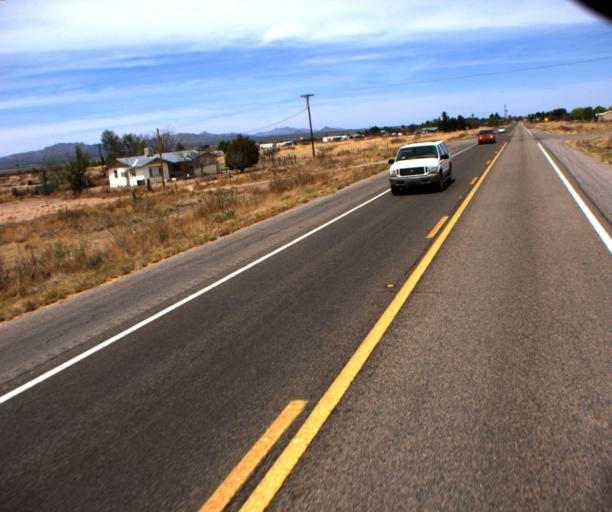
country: US
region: Arizona
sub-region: Cochise County
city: Bisbee
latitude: 31.6701
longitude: -109.6823
